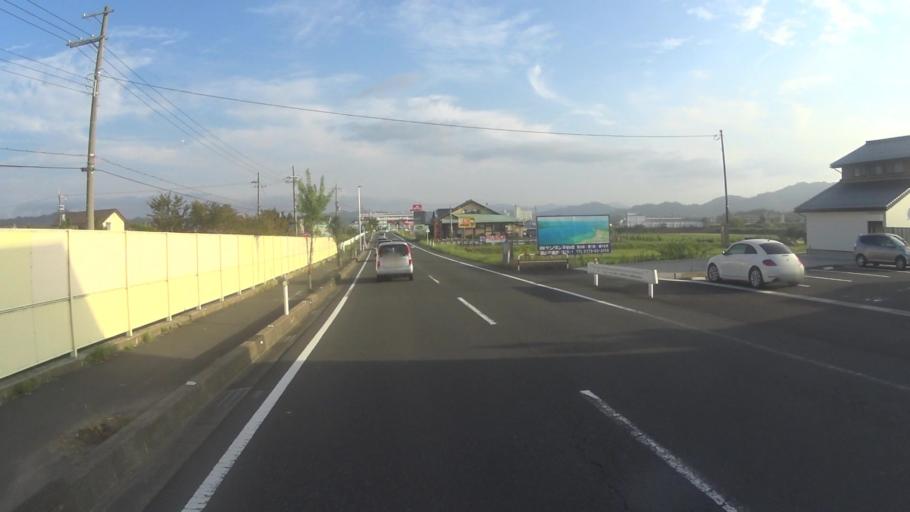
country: JP
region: Kyoto
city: Miyazu
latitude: 35.6140
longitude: 135.0786
